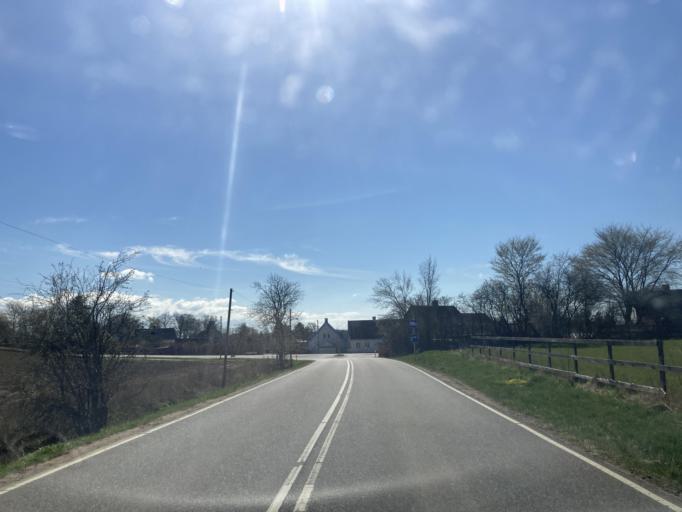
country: DK
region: Capital Region
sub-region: Gribskov Kommune
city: Helsinge
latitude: 56.0006
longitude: 12.2613
